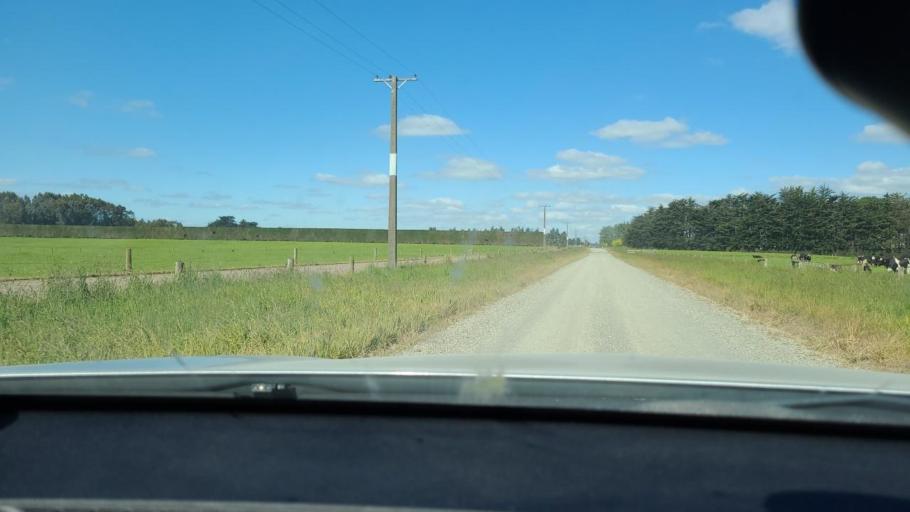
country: NZ
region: Southland
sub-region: Southland District
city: Riverton
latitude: -46.2712
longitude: 168.1707
